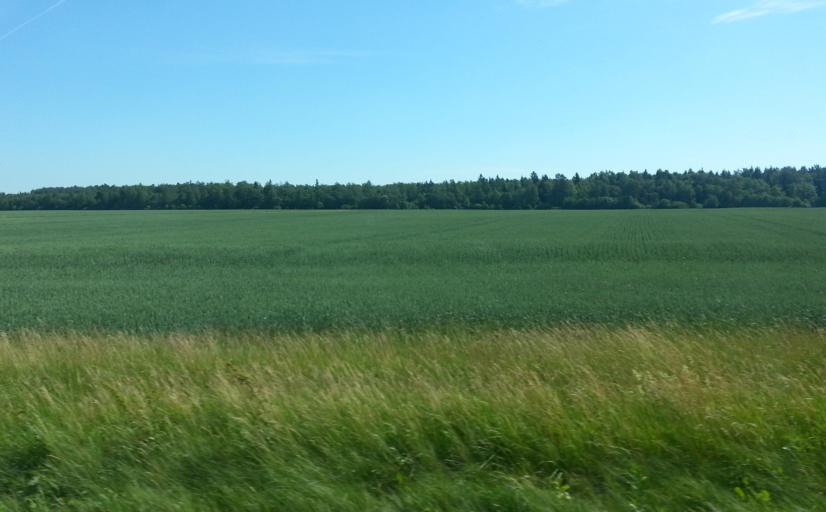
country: LT
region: Panevezys
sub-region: Panevezys City
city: Panevezys
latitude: 55.8387
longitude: 24.3593
